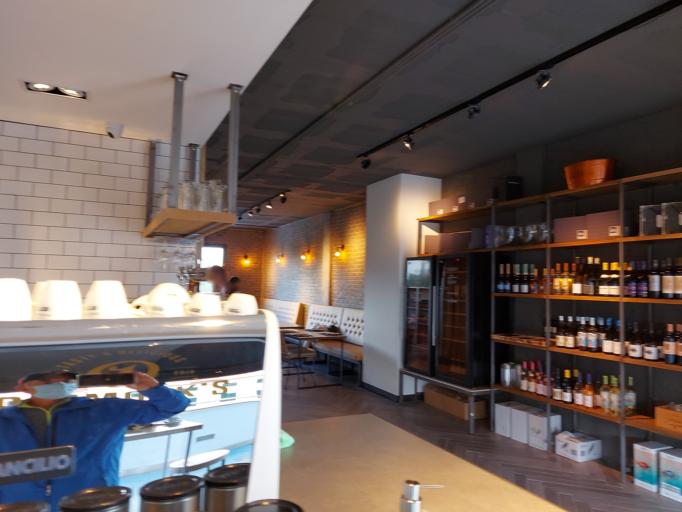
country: ES
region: Balearic Islands
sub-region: Illes Balears
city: s'Arenal
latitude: 39.4491
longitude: 2.7548
